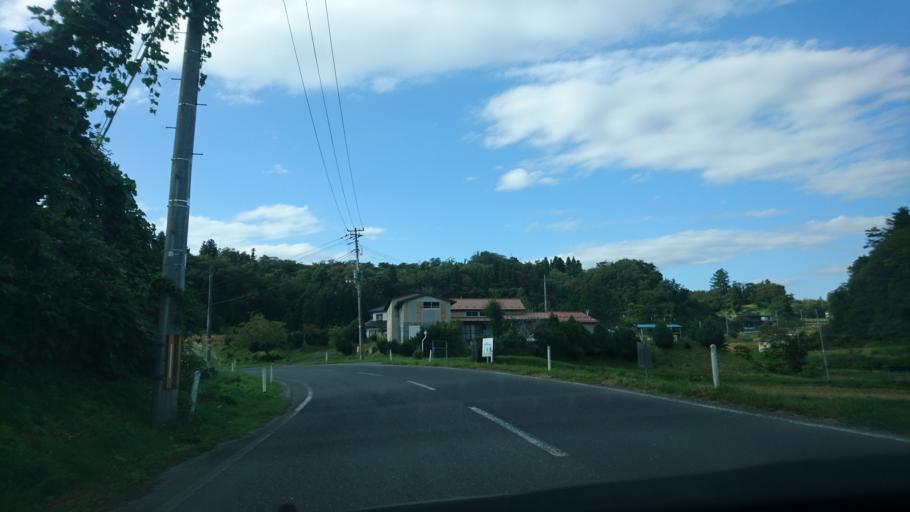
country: JP
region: Iwate
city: Ichinoseki
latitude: 38.8717
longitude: 141.3481
